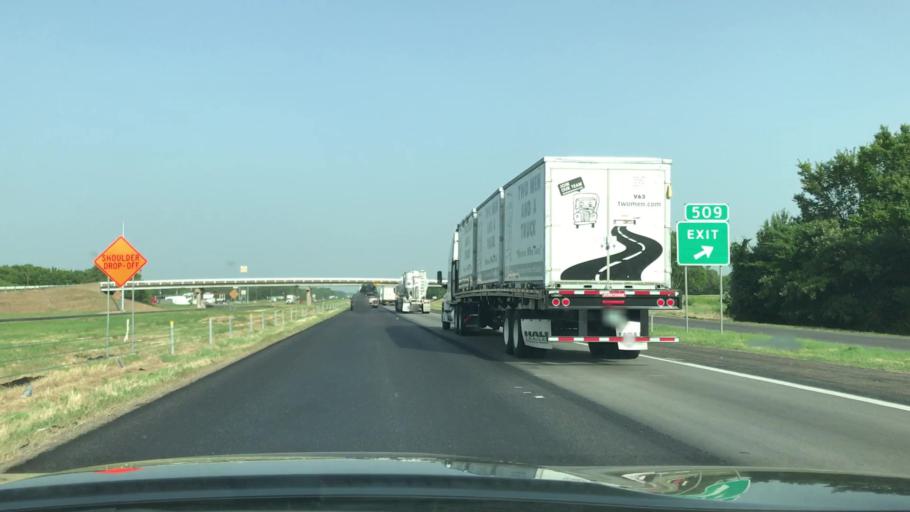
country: US
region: Texas
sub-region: Van Zandt County
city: Wills Point
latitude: 32.6686
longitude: -96.1437
